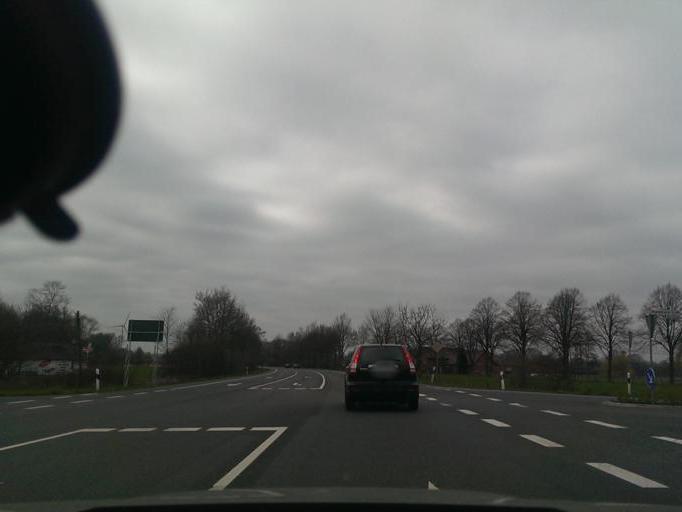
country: DE
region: North Rhine-Westphalia
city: Rietberg
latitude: 51.8176
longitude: 8.3995
